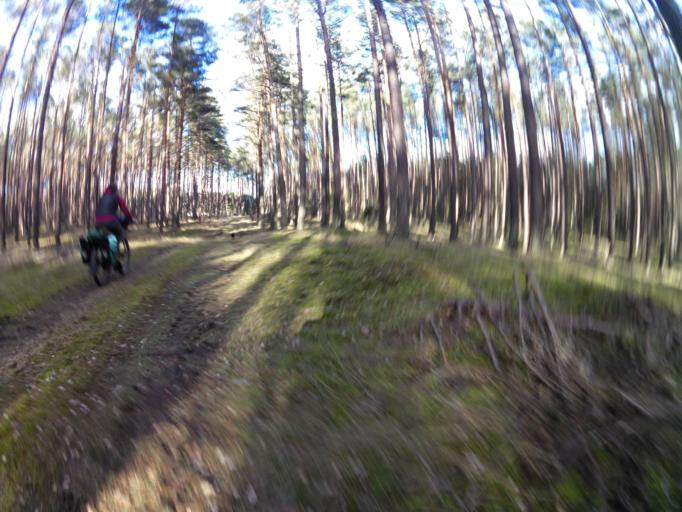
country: PL
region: West Pomeranian Voivodeship
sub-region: Powiat mysliborski
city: Debno
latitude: 52.7857
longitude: 14.7445
